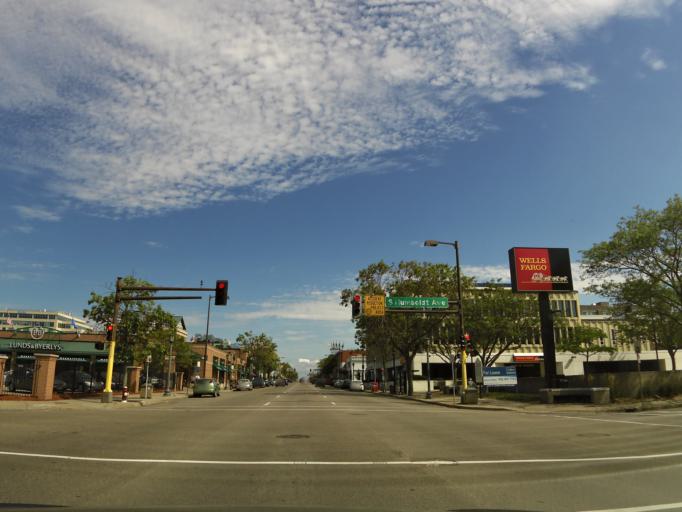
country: US
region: Minnesota
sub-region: Hennepin County
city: Saint Louis Park
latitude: 44.9484
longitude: -93.3011
